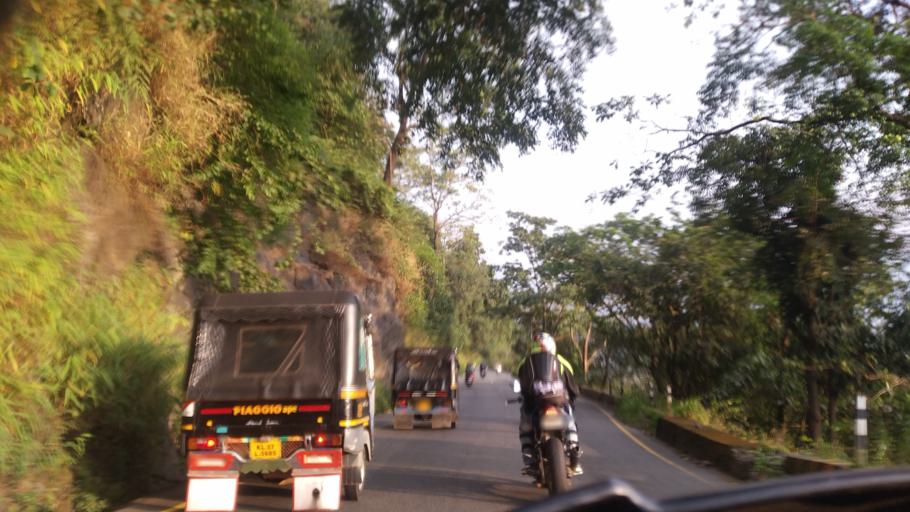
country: IN
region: Kerala
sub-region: Wayanad
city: Kalpetta
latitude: 11.5118
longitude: 76.0156
